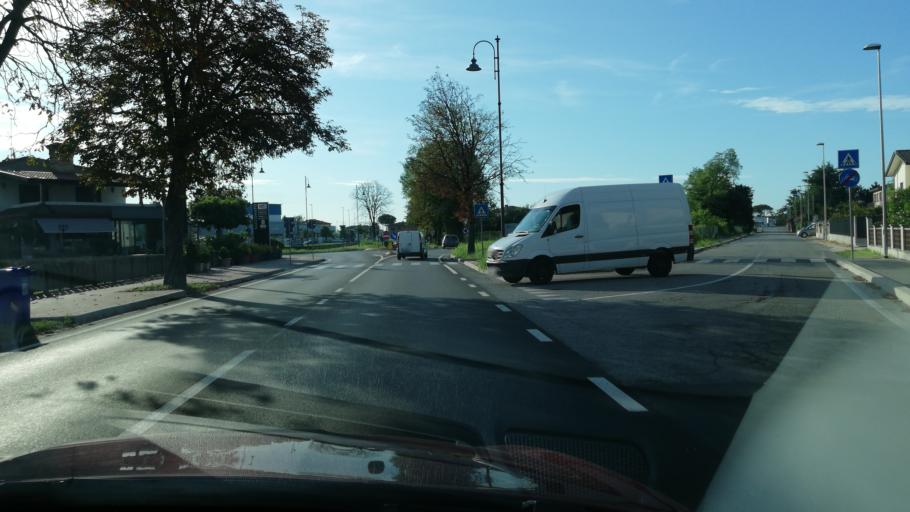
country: IT
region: Veneto
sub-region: Provincia di Venezia
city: Santo Stino di Livenza
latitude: 45.7237
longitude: 12.6968
